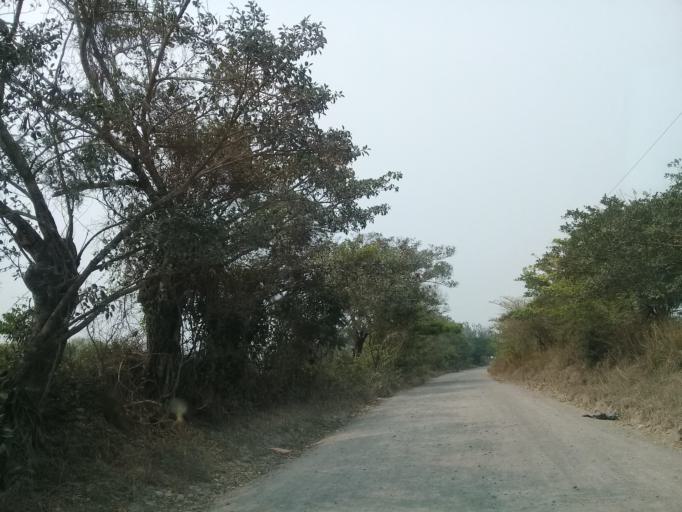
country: MX
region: Veracruz
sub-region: Medellin
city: La Laguna y Monte del Castillo
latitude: 18.9500
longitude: -96.1263
